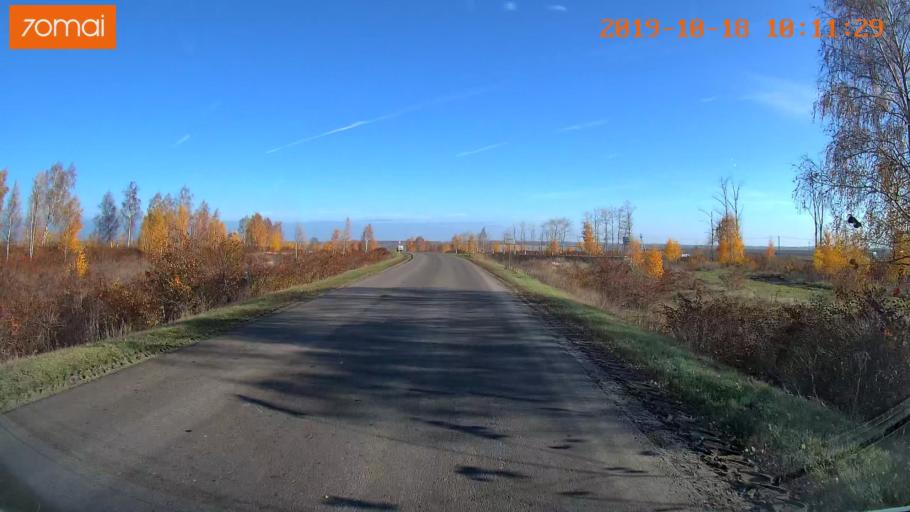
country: RU
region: Tula
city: Kurkino
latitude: 53.3826
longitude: 38.4990
